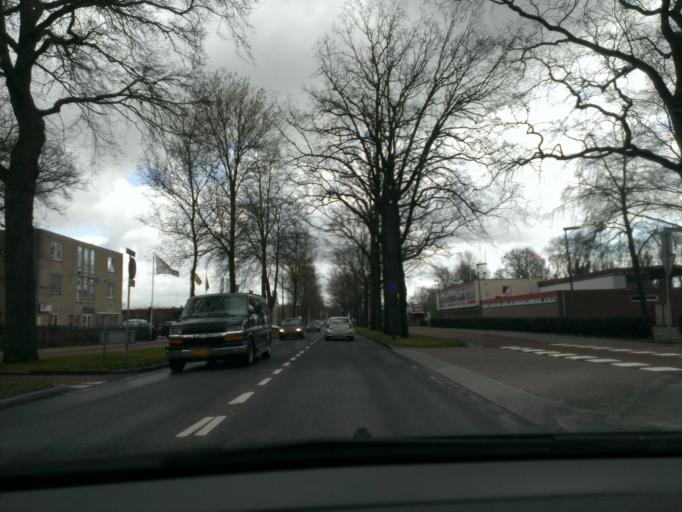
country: NL
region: Gelderland
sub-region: Gemeente Apeldoorn
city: Apeldoorn
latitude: 52.2351
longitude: 5.9705
